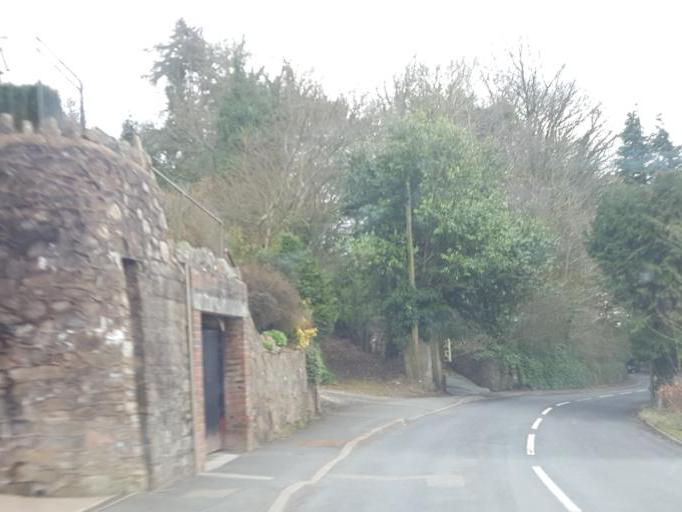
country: GB
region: England
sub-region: Worcestershire
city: Great Malvern
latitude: 52.0956
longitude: -2.3401
